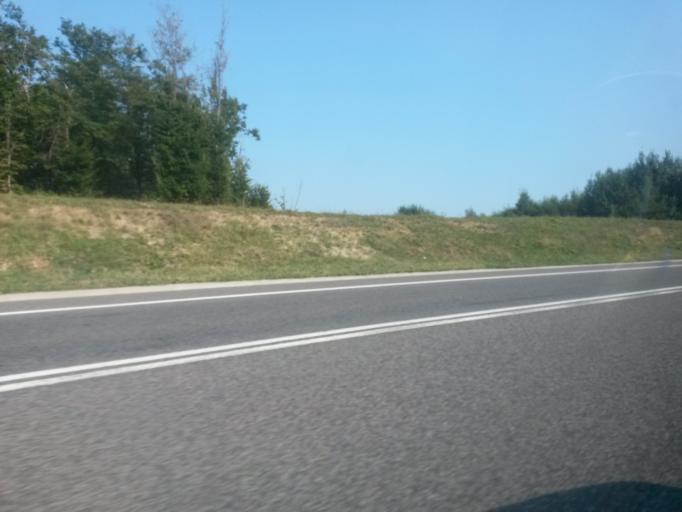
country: RO
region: Cluj
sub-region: Comuna Feleacu
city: Gheorghieni
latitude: 46.7165
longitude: 23.6623
